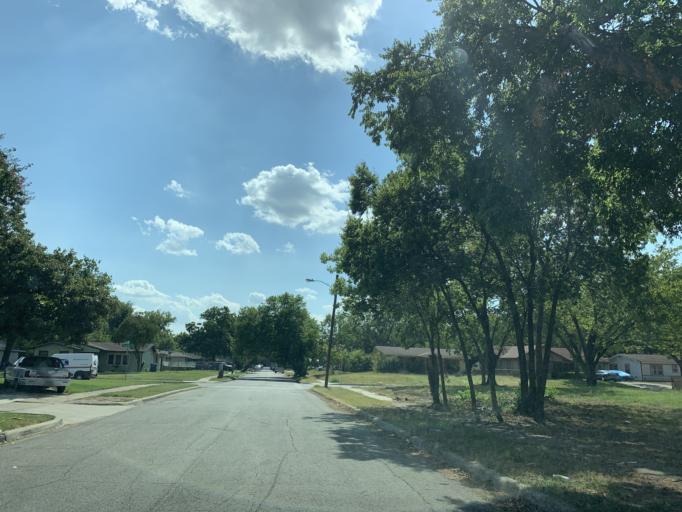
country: US
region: Texas
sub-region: Dallas County
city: Hutchins
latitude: 32.7015
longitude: -96.7716
